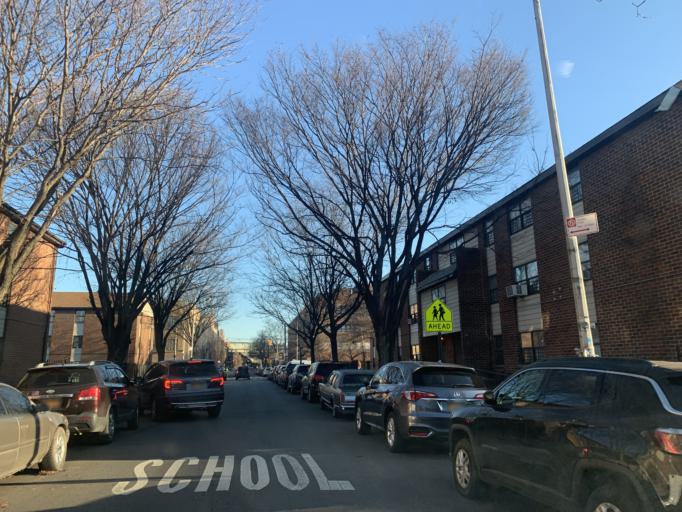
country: US
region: New York
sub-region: Kings County
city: East New York
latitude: 40.6969
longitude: -73.9207
